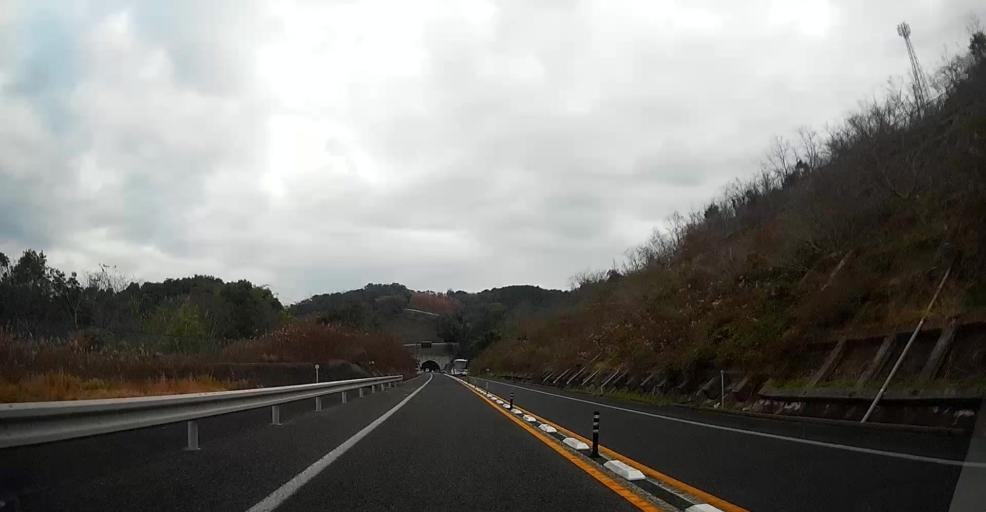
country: JP
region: Kumamoto
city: Hondo
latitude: 32.5085
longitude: 130.3308
